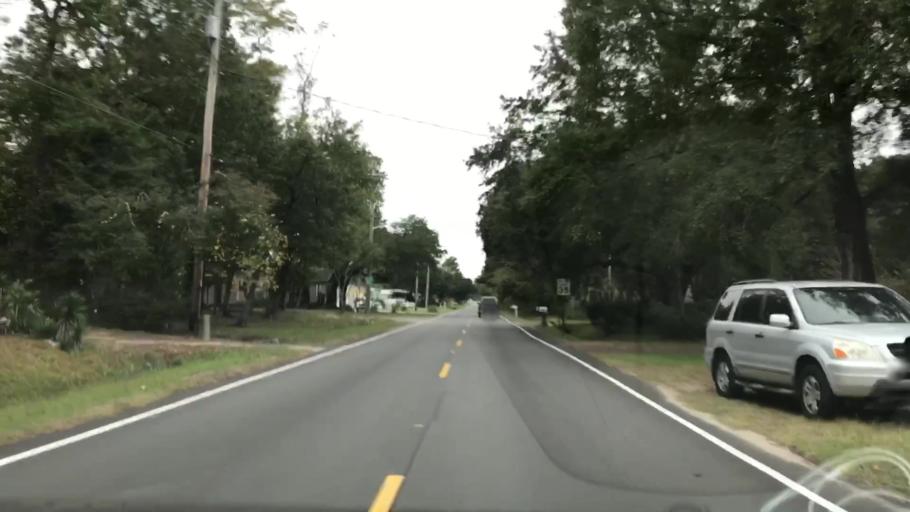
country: US
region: South Carolina
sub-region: Horry County
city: Garden City
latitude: 33.5859
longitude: -79.0010
